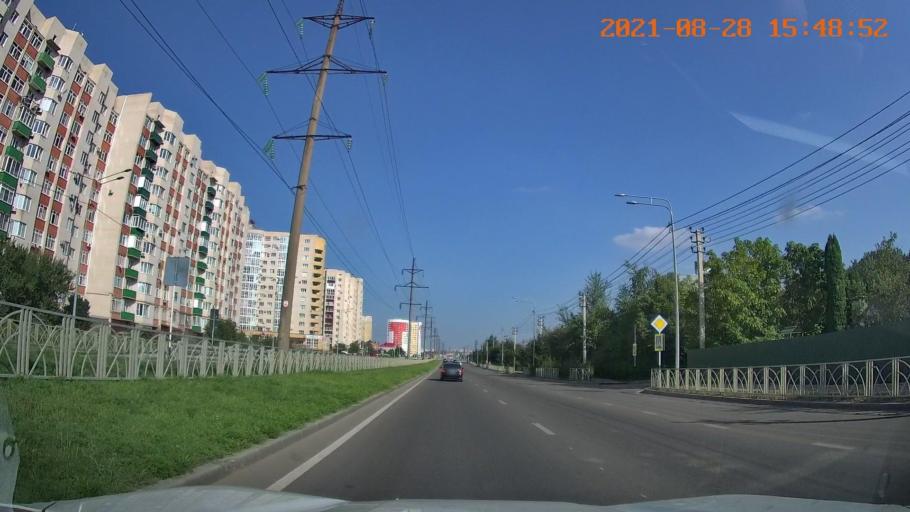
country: RU
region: Stavropol'skiy
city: Tatarka
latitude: 44.9958
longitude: 41.9129
